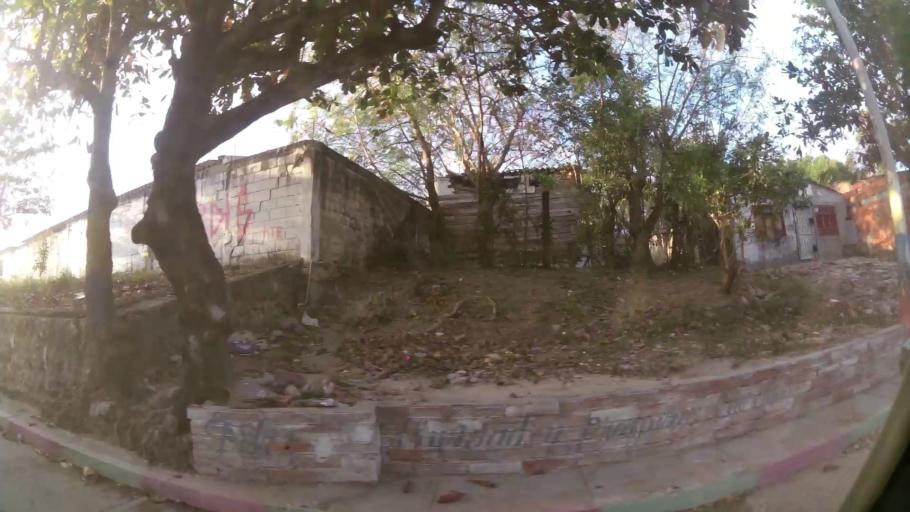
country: CO
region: Atlantico
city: Barranquilla
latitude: 10.9581
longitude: -74.8222
